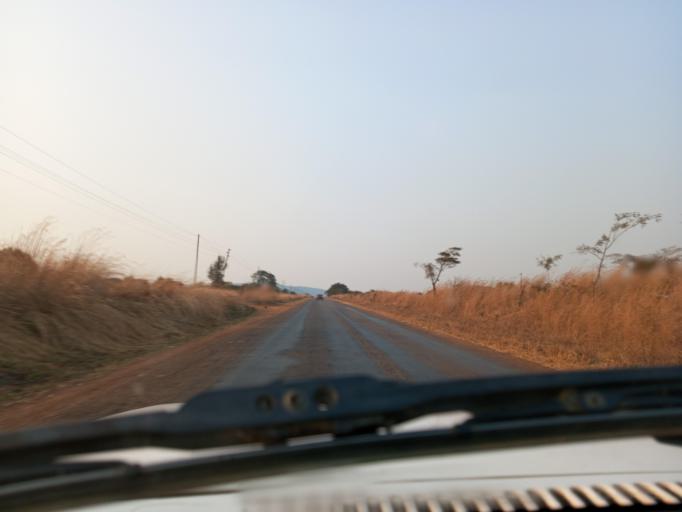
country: ZM
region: Northern
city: Mpika
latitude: -11.9057
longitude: 31.4142
